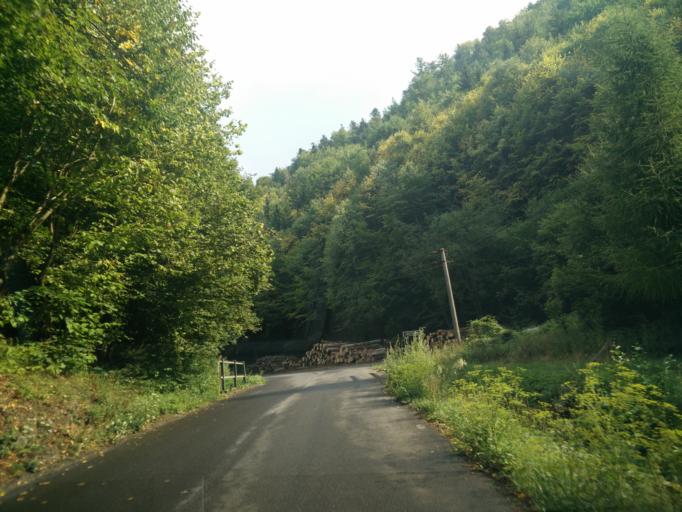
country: SK
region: Banskobystricky
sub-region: Okres Banska Bystrica
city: Banska Stiavnica
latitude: 48.4982
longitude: 18.8295
